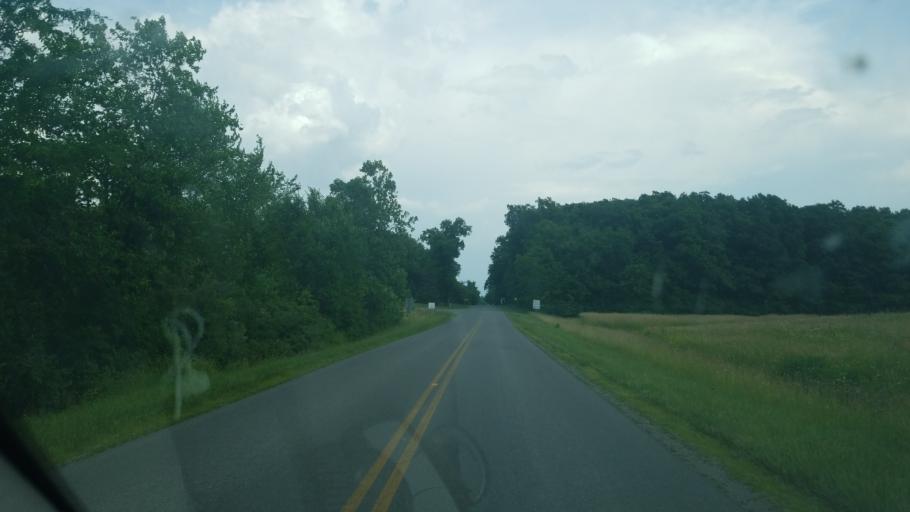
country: US
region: Ohio
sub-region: Logan County
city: Northwood
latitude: 40.4646
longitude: -83.6837
